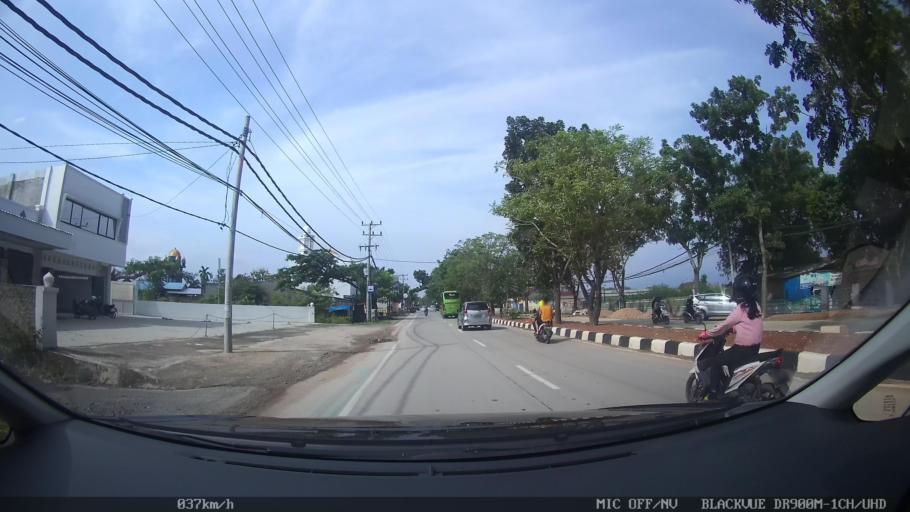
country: ID
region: Lampung
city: Kedaton
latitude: -5.3741
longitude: 105.2963
